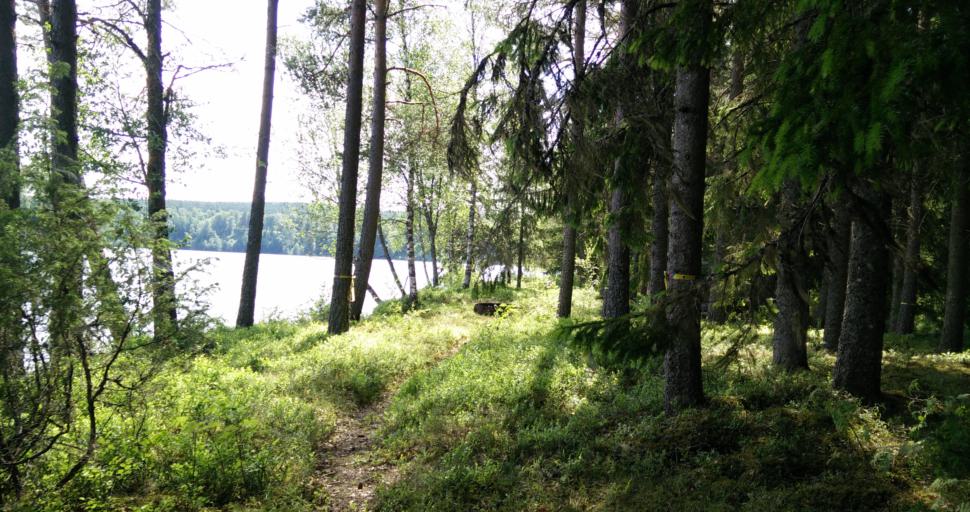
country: SE
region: Vaermland
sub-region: Hagfors Kommun
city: Hagfors
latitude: 59.9944
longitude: 13.5716
